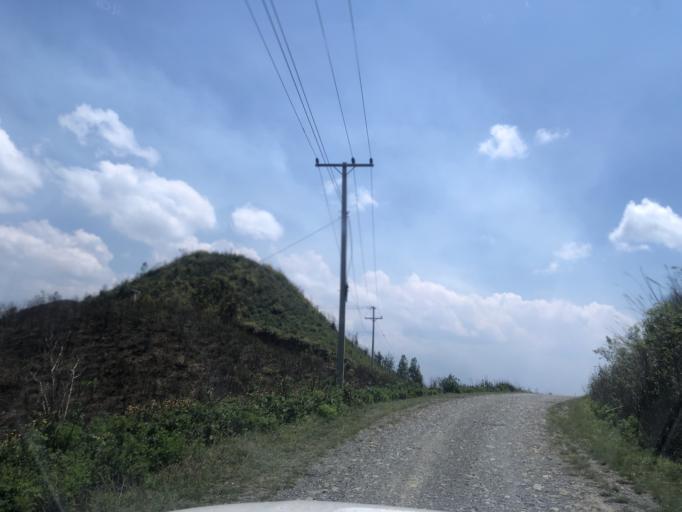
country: LA
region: Phongsali
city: Phongsali
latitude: 21.4158
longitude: 102.1853
